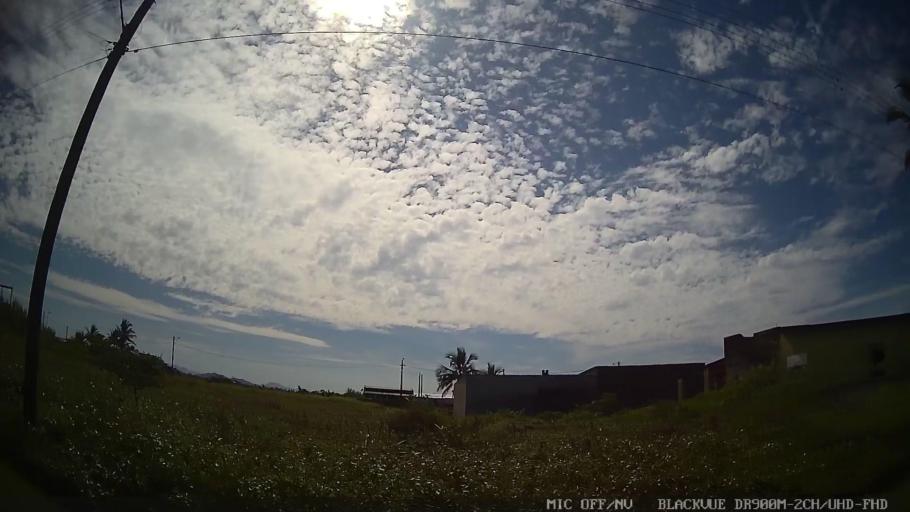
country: BR
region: Sao Paulo
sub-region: Iguape
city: Iguape
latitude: -24.7798
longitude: -47.6030
